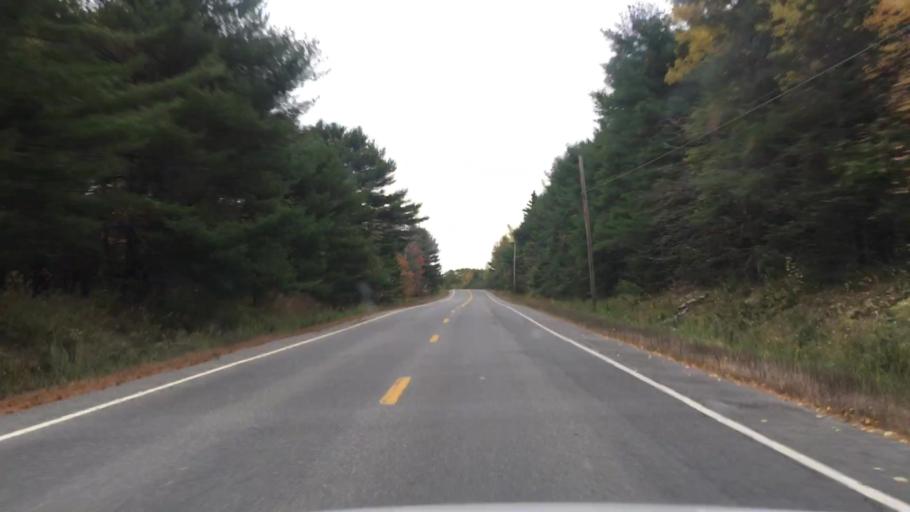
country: US
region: Maine
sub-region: Waldo County
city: Frankfort
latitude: 44.5570
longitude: -68.8554
